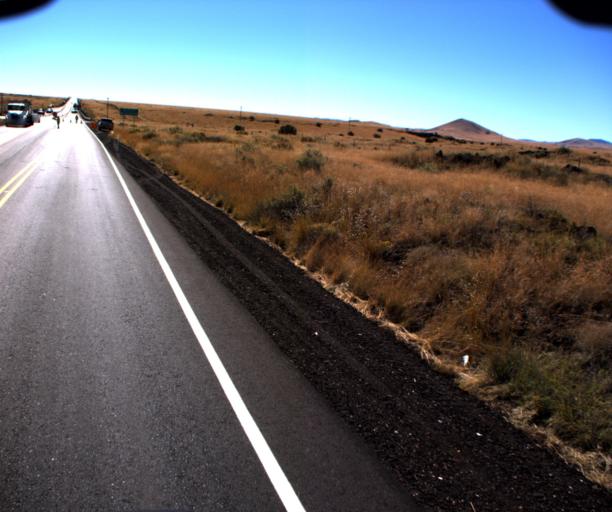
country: US
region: Arizona
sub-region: Apache County
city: Springerville
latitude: 34.2832
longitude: -109.3681
